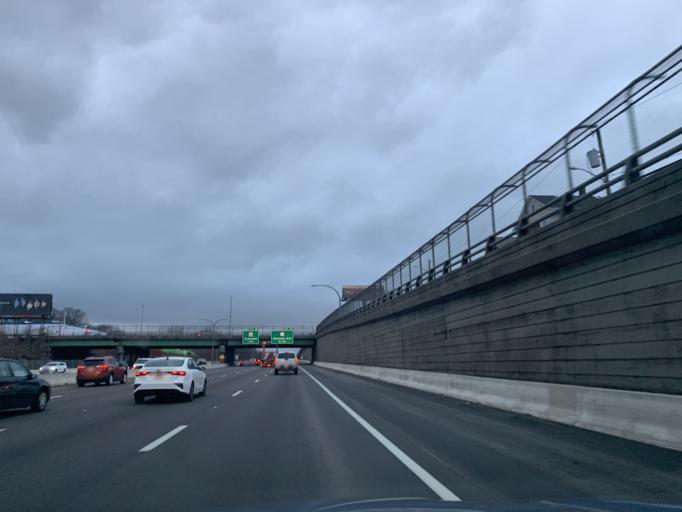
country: US
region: Rhode Island
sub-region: Providence County
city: Providence
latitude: 41.7952
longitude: -71.4082
